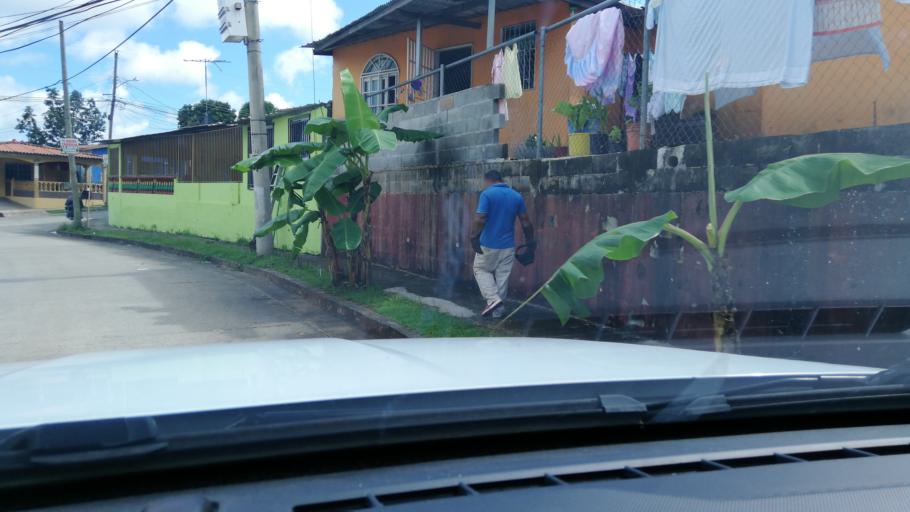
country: PA
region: Panama
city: Tocumen
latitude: 9.1091
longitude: -79.3778
